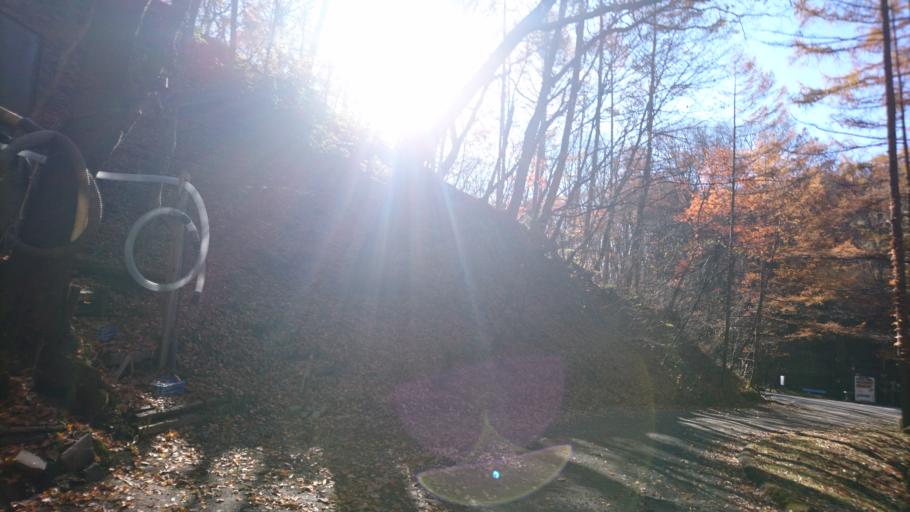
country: JP
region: Nagano
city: Komoro
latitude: 36.3887
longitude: 138.6137
